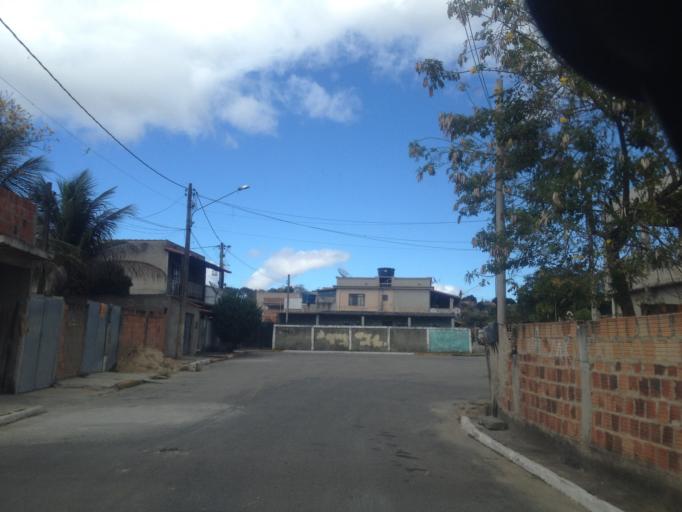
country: BR
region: Rio de Janeiro
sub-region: Porto Real
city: Porto Real
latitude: -22.4386
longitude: -44.3164
